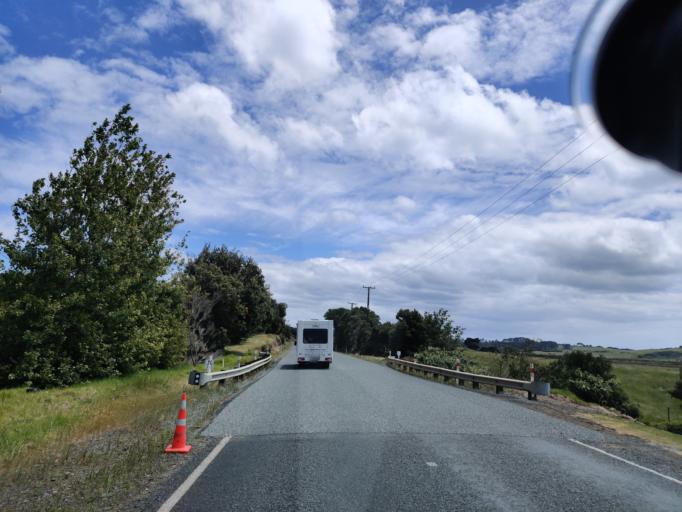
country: NZ
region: Northland
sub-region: Far North District
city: Kaitaia
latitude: -34.7768
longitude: 173.0930
